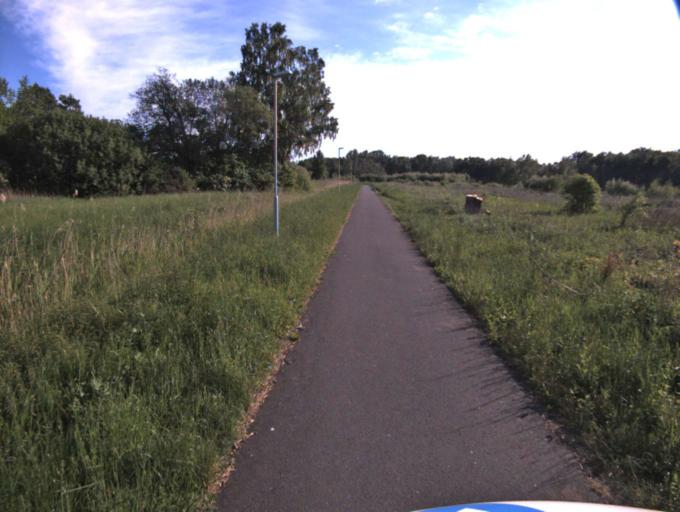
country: SE
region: Skane
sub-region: Kristianstads Kommun
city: Kristianstad
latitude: 56.0456
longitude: 14.1942
